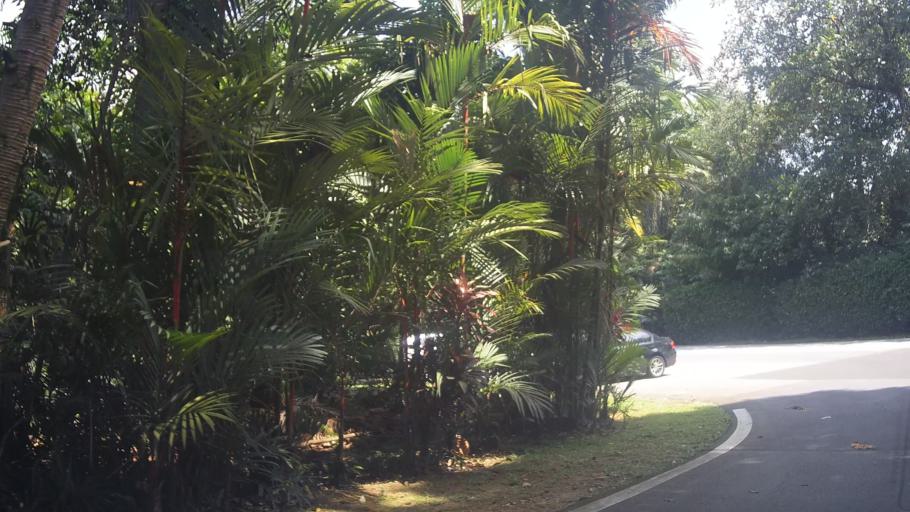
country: SG
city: Singapore
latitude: 1.3510
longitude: 103.7668
